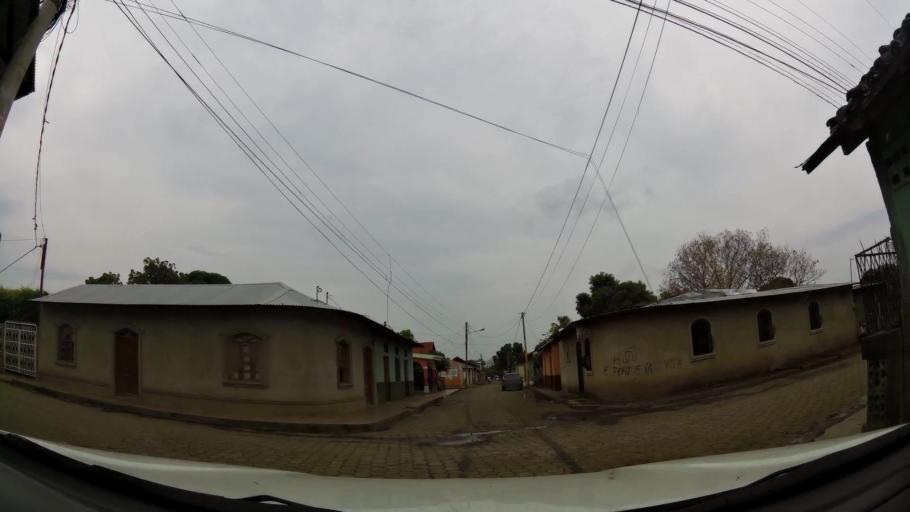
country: NI
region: Granada
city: Nandaime
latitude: 11.7577
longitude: -86.0488
